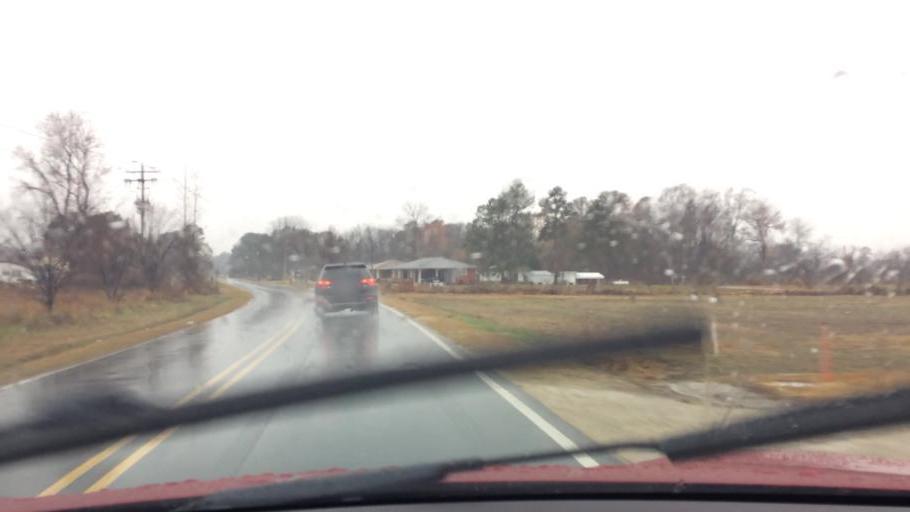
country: US
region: North Carolina
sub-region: Wayne County
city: Goldsboro
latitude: 35.4122
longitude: -77.9271
